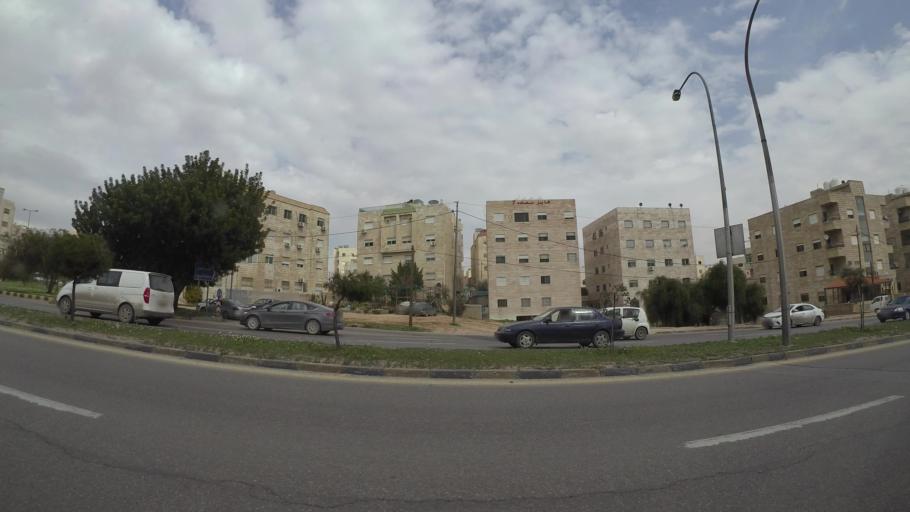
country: JO
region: Amman
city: Amman
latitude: 31.9713
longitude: 35.9391
